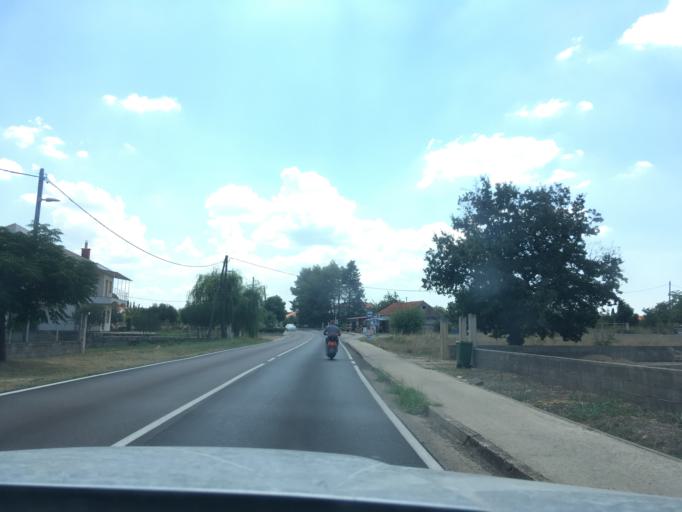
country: HR
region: Zadarska
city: Policnik
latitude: 44.1604
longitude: 15.3087
